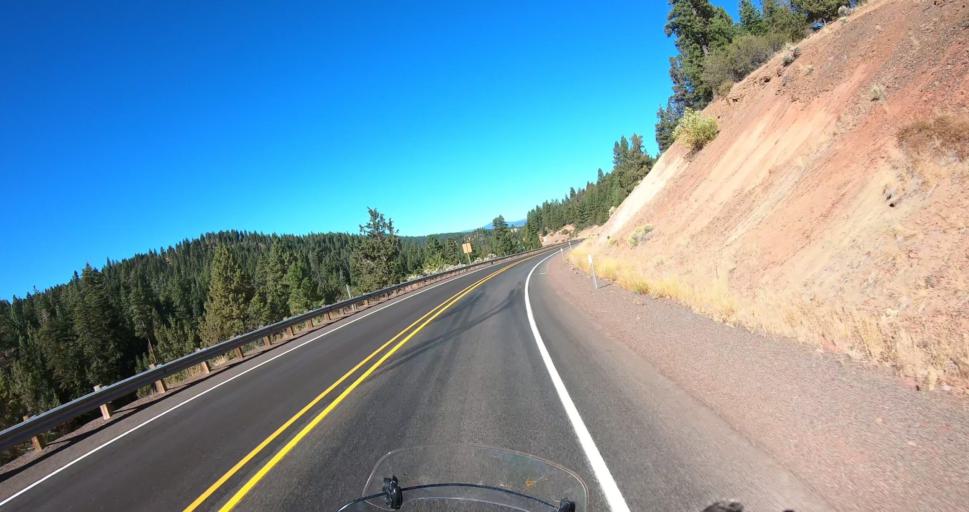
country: US
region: Oregon
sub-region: Lake County
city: Lakeview
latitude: 42.2383
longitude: -120.3003
